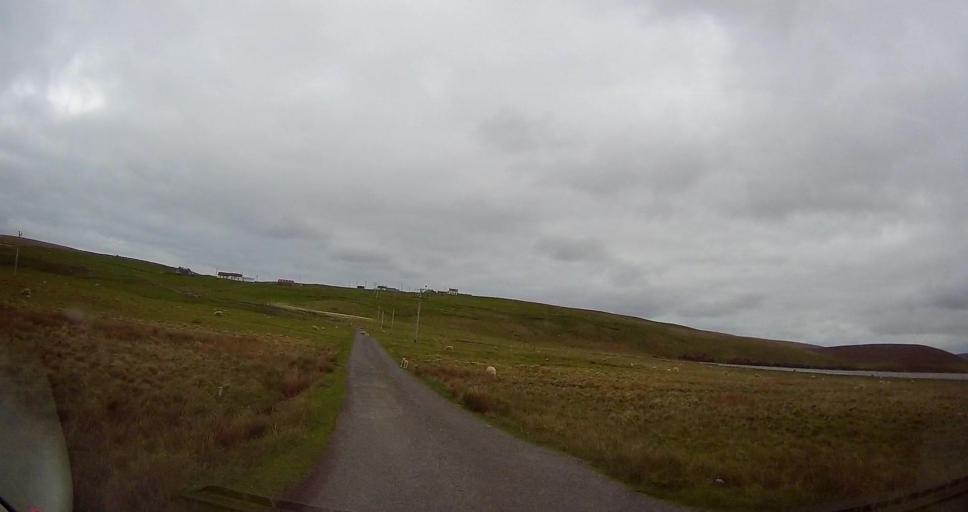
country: GB
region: Scotland
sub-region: Shetland Islands
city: Shetland
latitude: 60.8042
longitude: -0.8854
